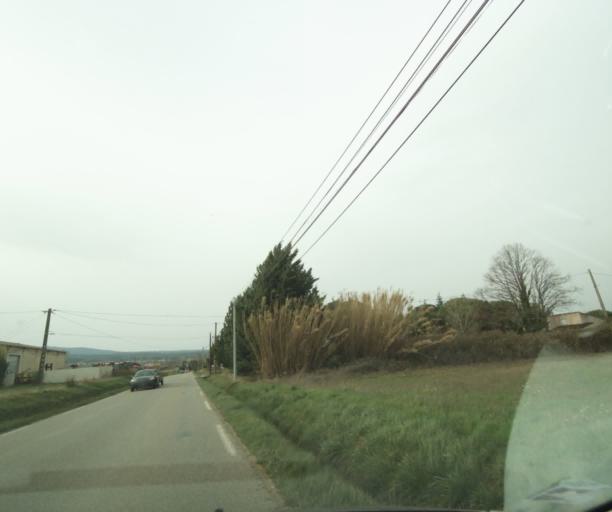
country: FR
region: Provence-Alpes-Cote d'Azur
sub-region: Departement des Bouches-du-Rhone
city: Trets
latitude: 43.4562
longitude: 5.6963
